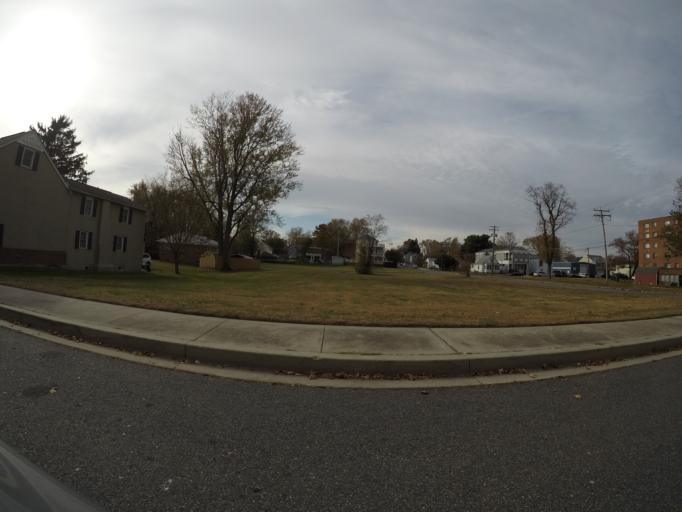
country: US
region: Maryland
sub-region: Harford County
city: Havre de Grace
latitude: 39.5423
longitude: -76.0855
